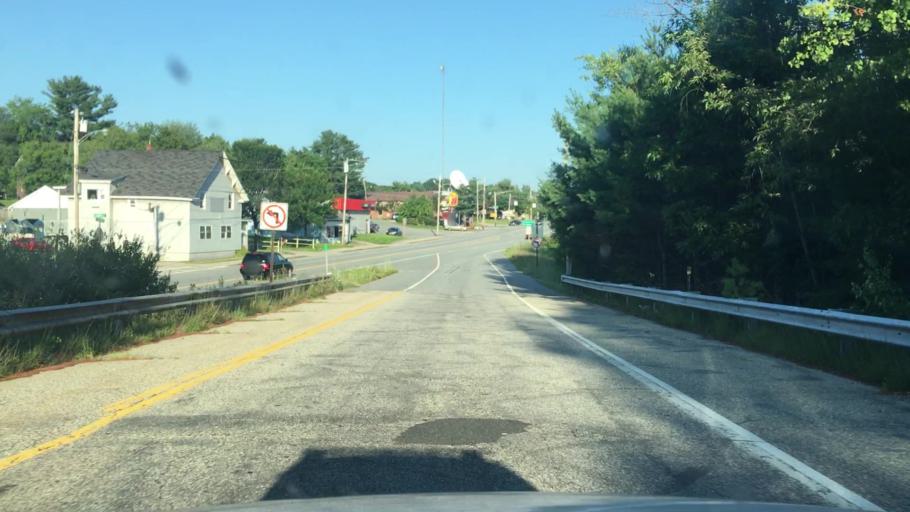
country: US
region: Maine
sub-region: Androscoggin County
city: Lewiston
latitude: 44.0746
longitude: -70.1809
